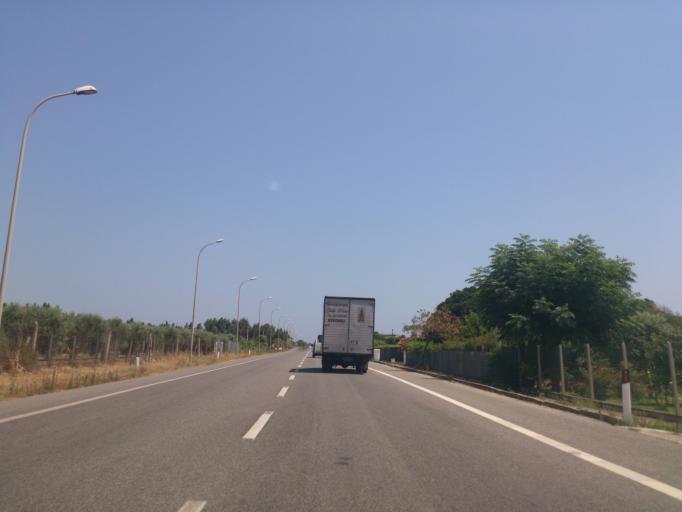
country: IT
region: Calabria
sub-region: Provincia di Reggio Calabria
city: Monasterace Marina
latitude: 38.4145
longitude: 16.5578
